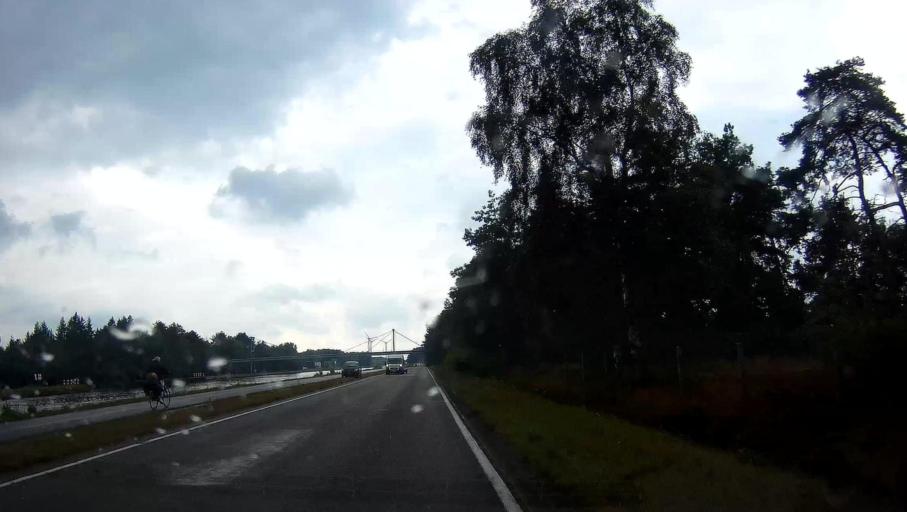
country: BE
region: Flanders
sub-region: Provincie Antwerpen
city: Dessel
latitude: 51.2259
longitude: 5.1628
